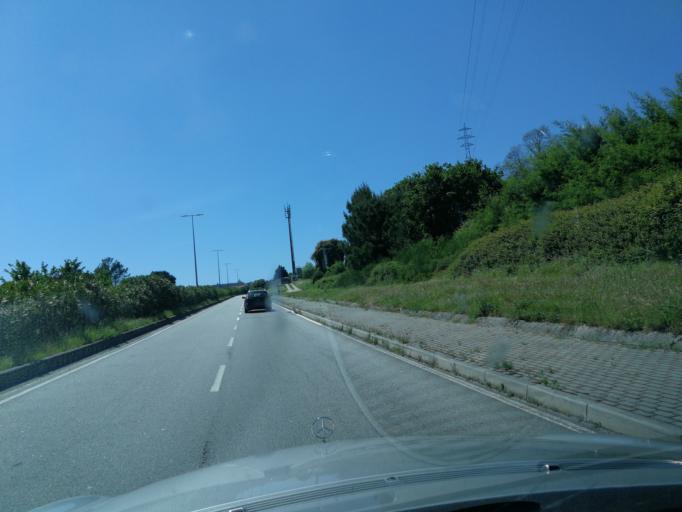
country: PT
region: Viana do Castelo
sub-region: Viana do Castelo
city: Meadela
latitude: 41.7101
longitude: -8.8035
